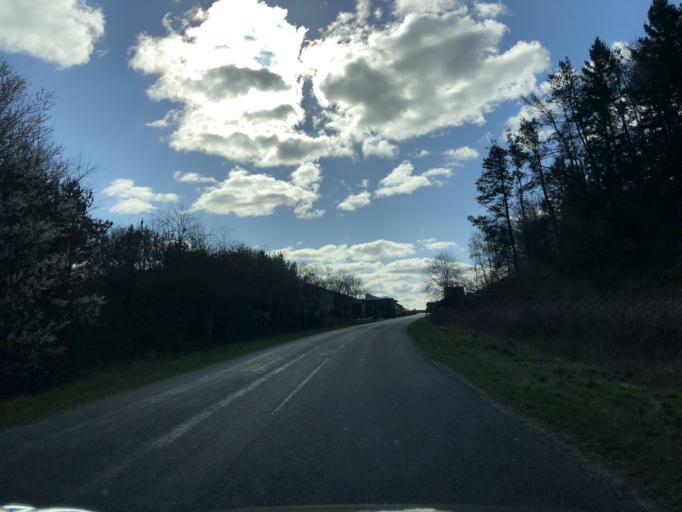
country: DK
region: North Denmark
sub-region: Vesthimmerland Kommune
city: Alestrup
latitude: 56.6108
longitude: 9.5368
